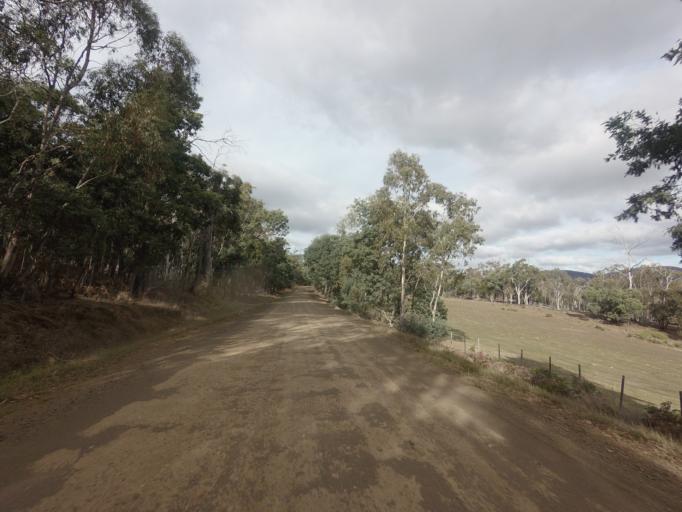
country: AU
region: Tasmania
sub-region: Brighton
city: Bridgewater
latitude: -42.4604
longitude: 147.2632
